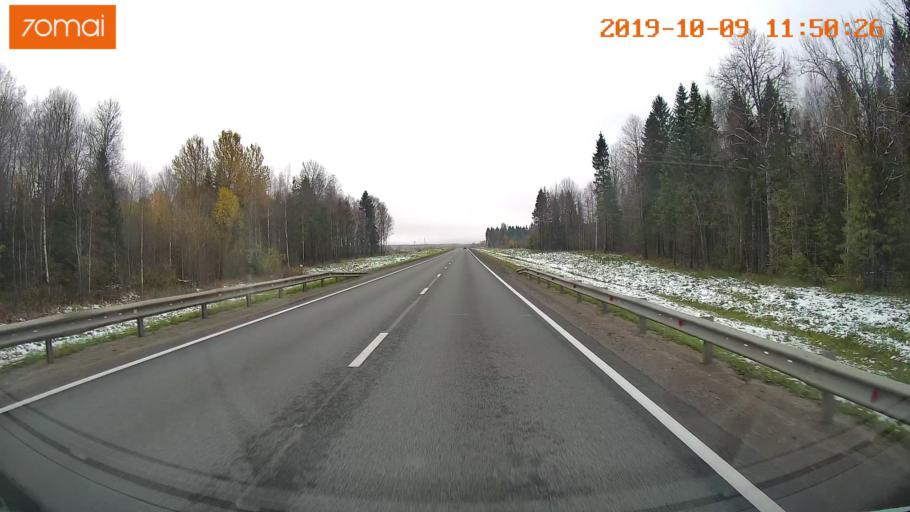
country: RU
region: Vologda
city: Gryazovets
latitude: 58.8055
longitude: 40.2464
